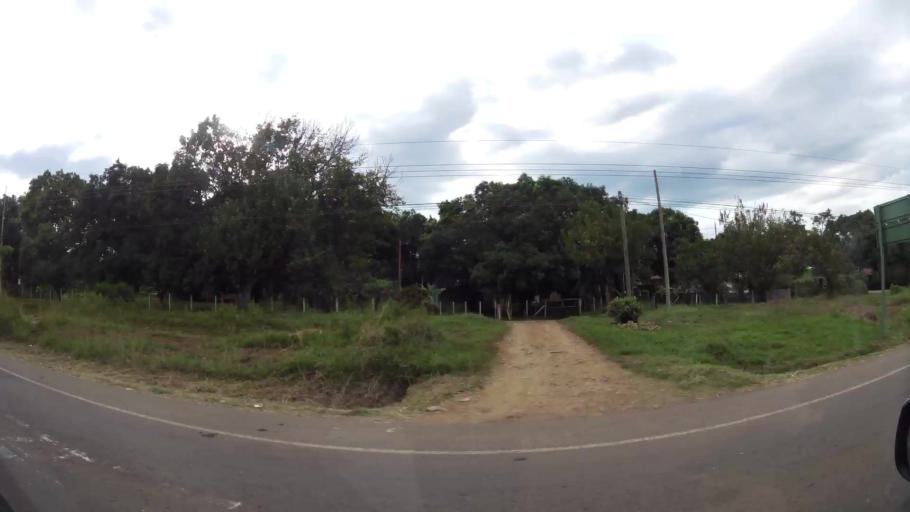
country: CR
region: Alajuela
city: Orotina
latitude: 9.8840
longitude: -84.5759
